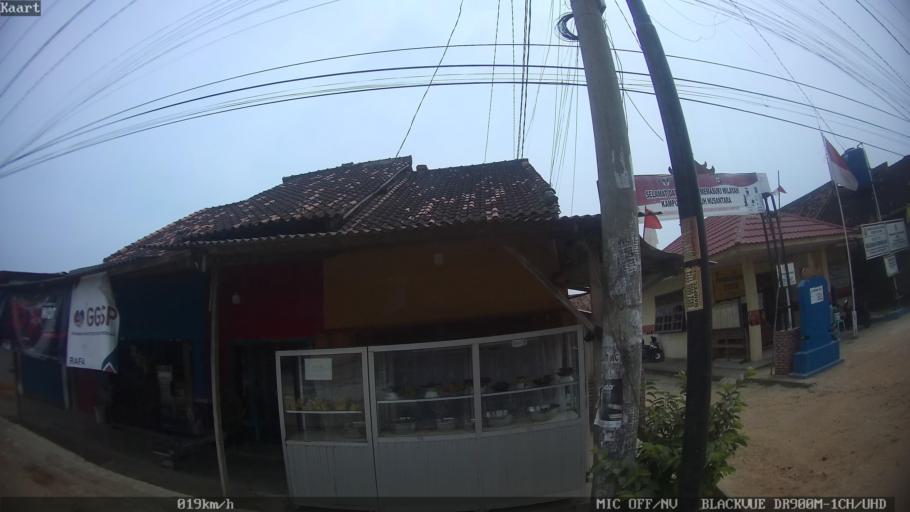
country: ID
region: Lampung
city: Bandarlampung
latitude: -5.4066
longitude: 105.3012
